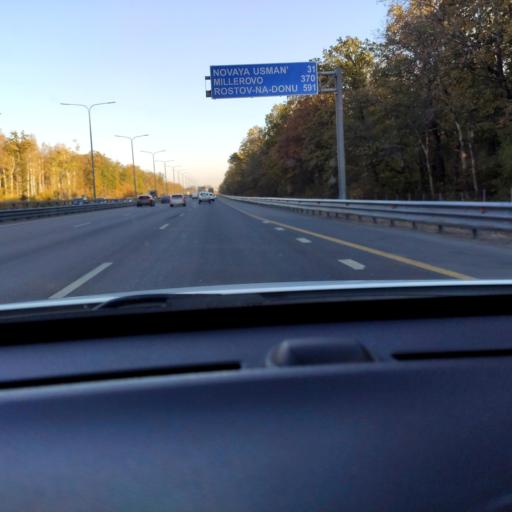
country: RU
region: Voronezj
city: Podgornoye
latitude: 51.8362
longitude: 39.2257
